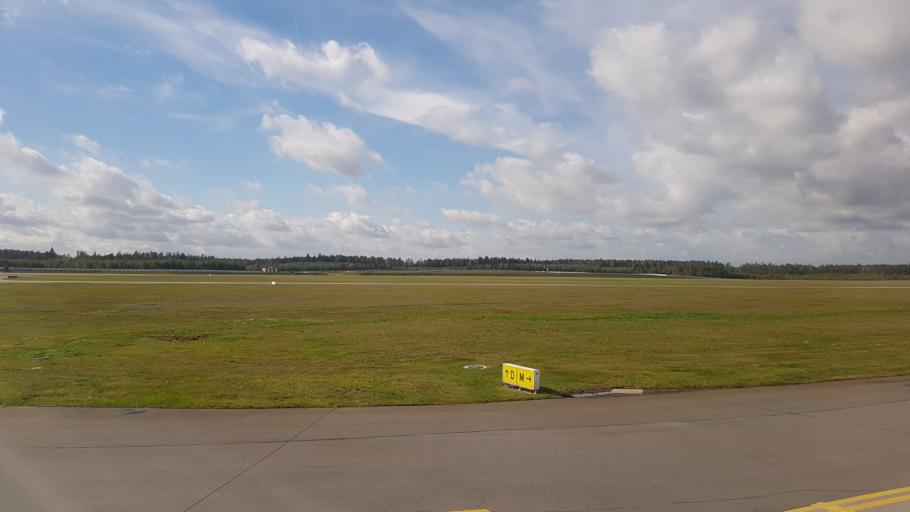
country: BY
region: Minsk
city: Smilavichy
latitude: 53.8851
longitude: 28.0344
